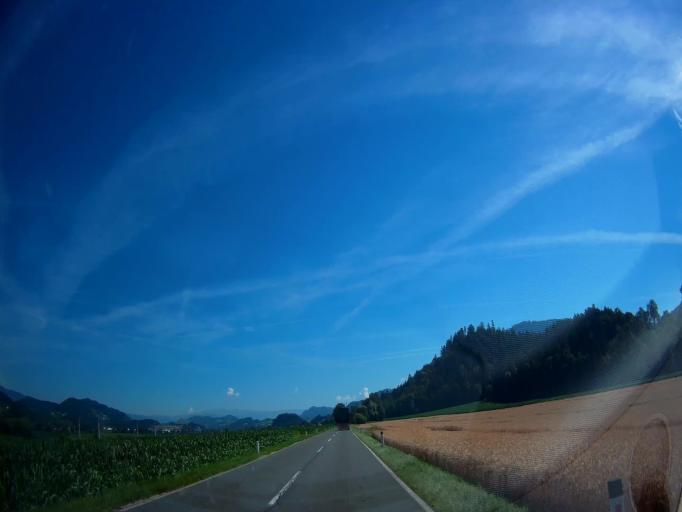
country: AT
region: Carinthia
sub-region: Politischer Bezirk Klagenfurt Land
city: Maria Saal
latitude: 46.7062
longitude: 14.3646
